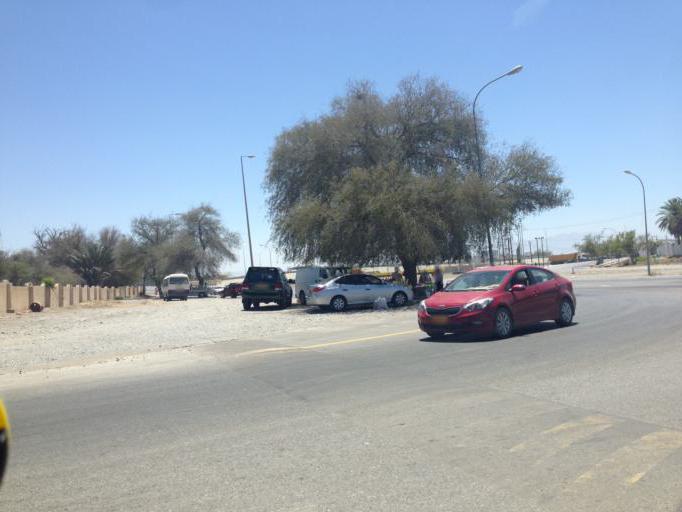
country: OM
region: Muhafazat Masqat
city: As Sib al Jadidah
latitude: 23.6636
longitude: 58.2043
